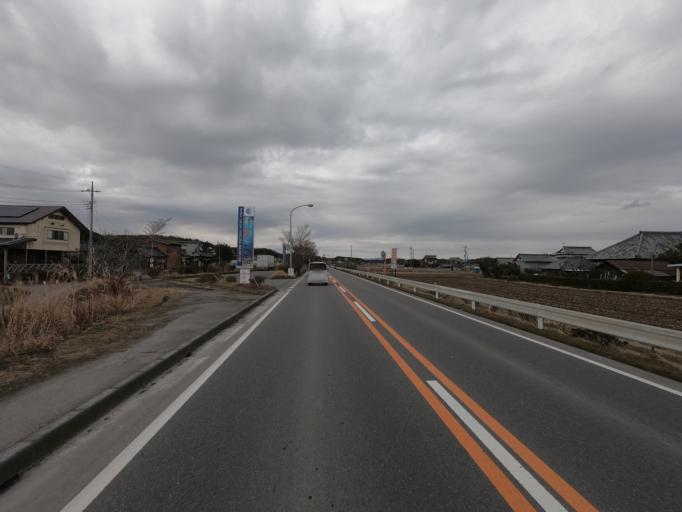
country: JP
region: Ibaraki
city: Inashiki
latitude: 36.0899
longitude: 140.3836
